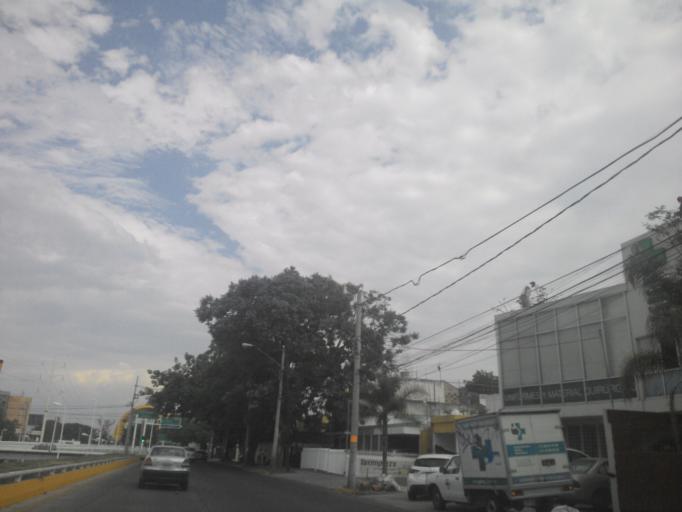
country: MX
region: Jalisco
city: Guadalajara
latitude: 20.6618
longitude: -103.3887
